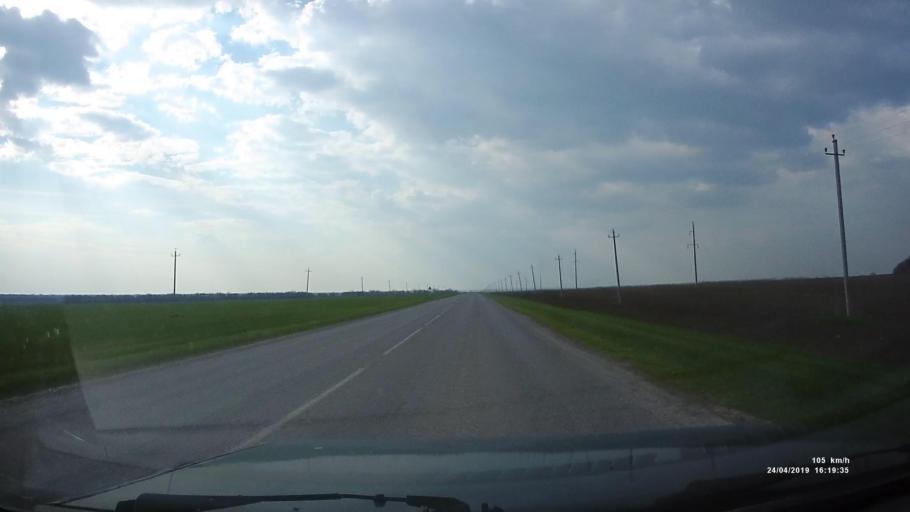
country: RU
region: Rostov
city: Sovetskoye
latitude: 46.7831
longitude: 42.0942
